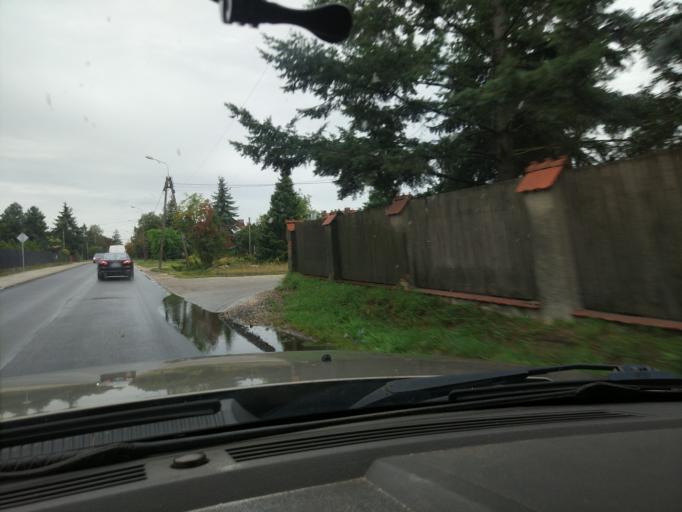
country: PL
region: Masovian Voivodeship
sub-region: Powiat warszawski zachodni
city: Ozarow Mazowiecki
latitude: 52.1886
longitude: 20.7602
